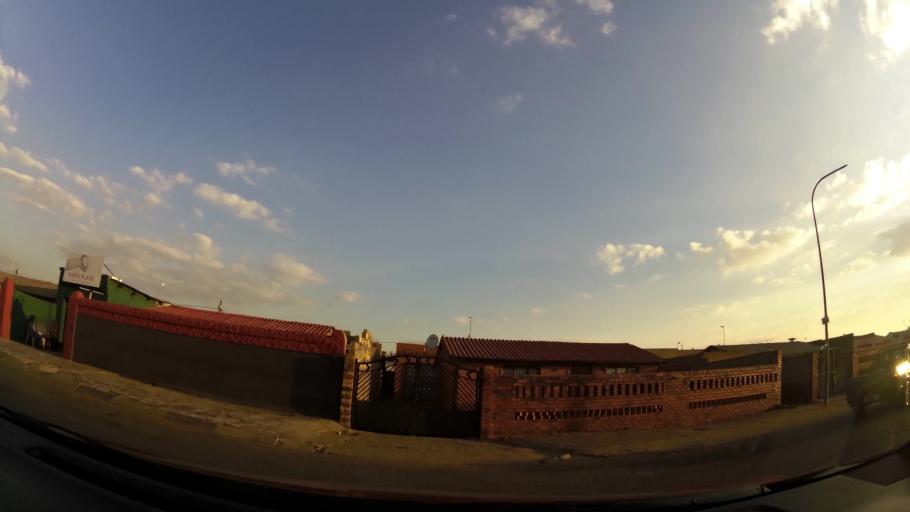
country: ZA
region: Gauteng
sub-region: City of Johannesburg Metropolitan Municipality
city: Roodepoort
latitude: -26.2126
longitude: 27.8965
